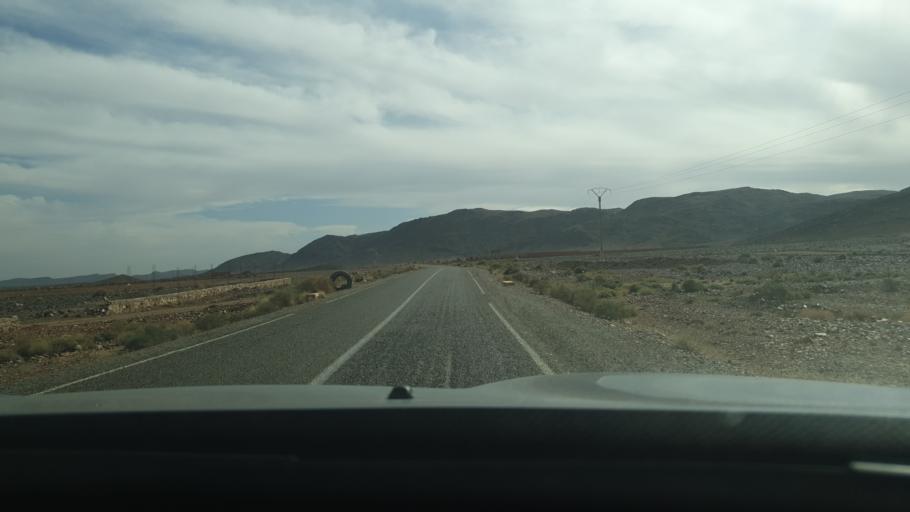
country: MA
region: Meknes-Tafilalet
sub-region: Errachidia
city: Fezna
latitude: 31.5305
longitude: -4.6391
